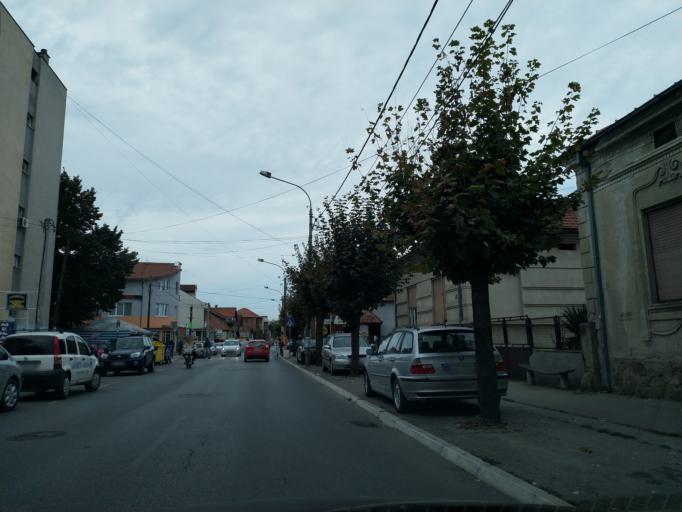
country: RS
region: Central Serbia
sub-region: Pomoravski Okrug
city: Jagodina
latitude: 43.9819
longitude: 21.2552
